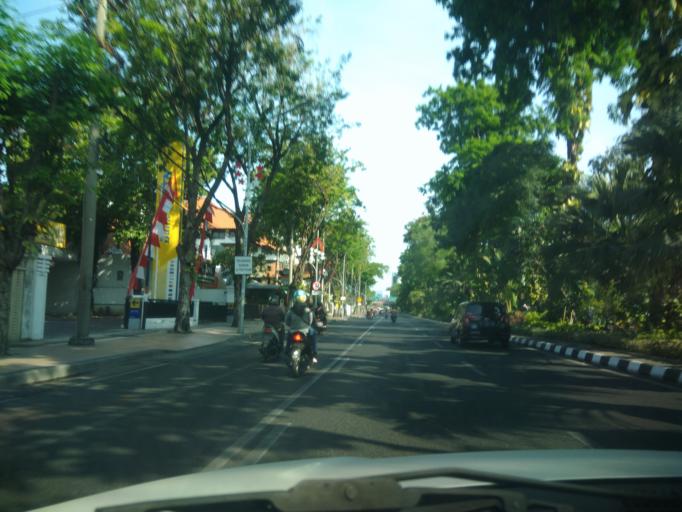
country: ID
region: East Java
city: Jagirsidosermo
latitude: -7.2930
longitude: 112.7391
